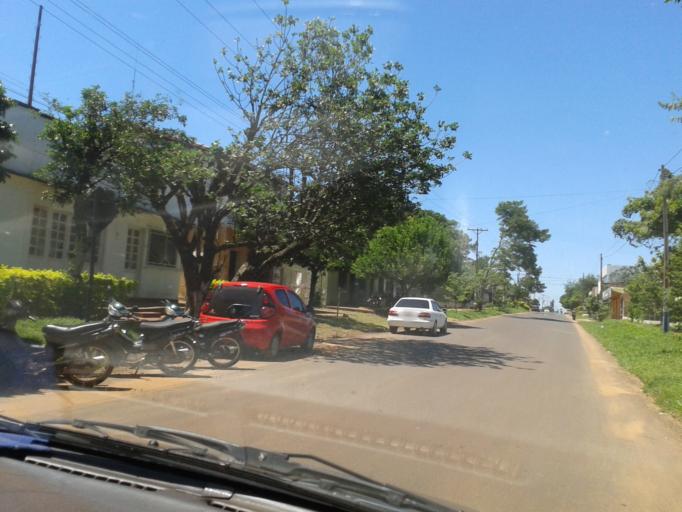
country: PY
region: Misiones
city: Santa Maria
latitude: -26.8883
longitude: -57.0260
